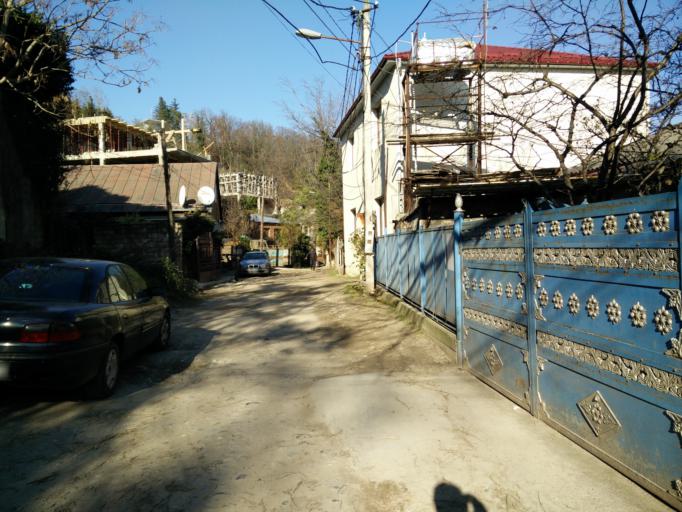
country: GE
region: Imereti
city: Kutaisi
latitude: 42.2687
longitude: 42.6992
